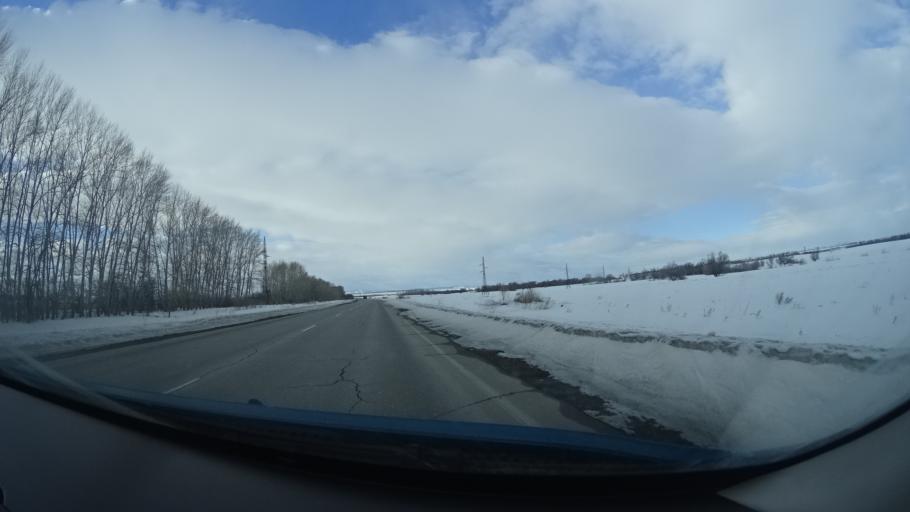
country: RU
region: Chelyabinsk
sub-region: Gorod Magnitogorsk
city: Magnitogorsk
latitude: 53.5732
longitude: 58.8934
